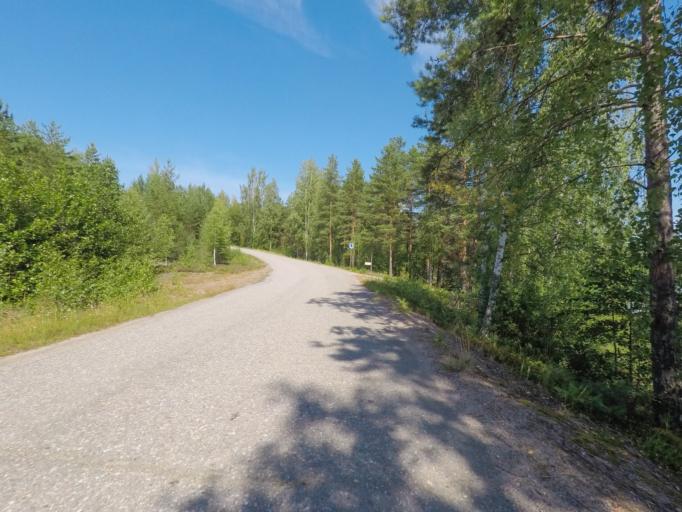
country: FI
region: Southern Savonia
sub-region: Mikkeli
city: Puumala
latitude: 61.4099
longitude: 28.0921
